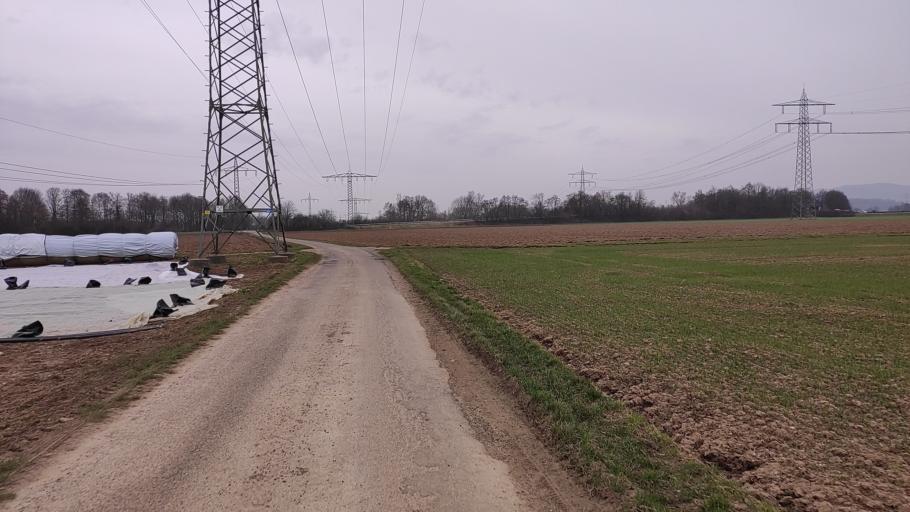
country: DE
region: Baden-Wuerttemberg
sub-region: Freiburg Region
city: Riegel
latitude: 48.1708
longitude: 7.7563
